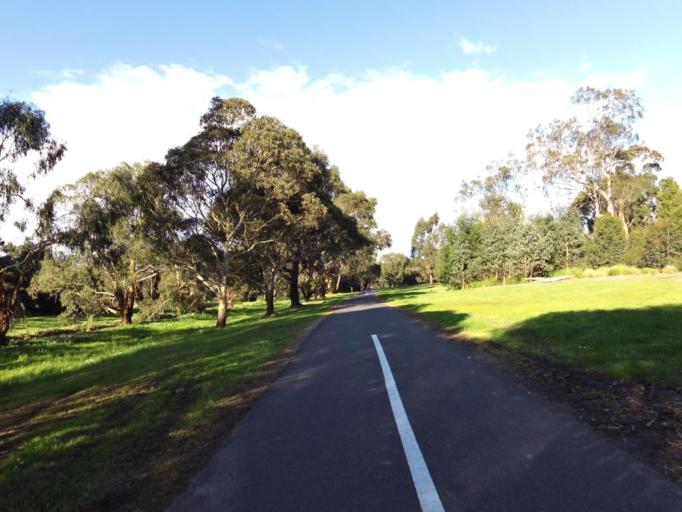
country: AU
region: Victoria
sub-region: Knox
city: Wantirna
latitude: -37.8381
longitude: 145.2214
